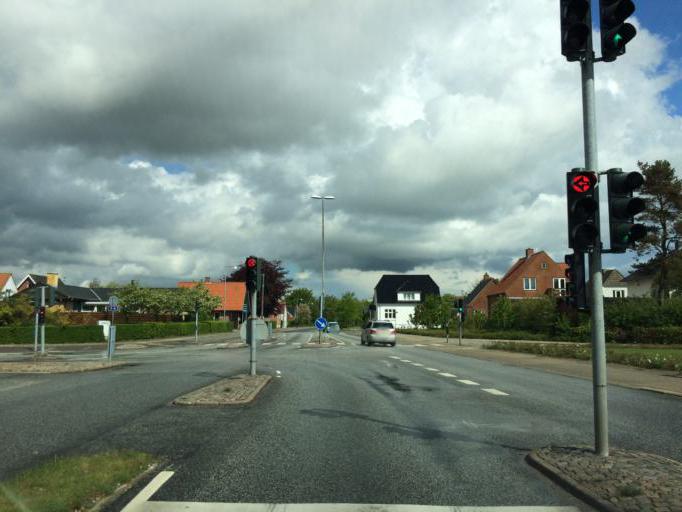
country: DK
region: Central Jutland
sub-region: Holstebro Kommune
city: Holstebro
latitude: 56.3649
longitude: 8.6114
